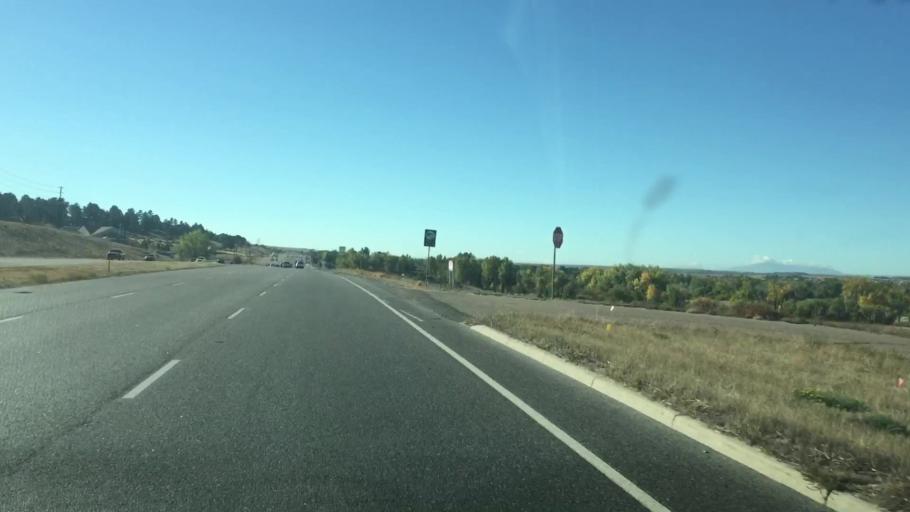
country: US
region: Colorado
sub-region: Douglas County
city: Parker
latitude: 39.5069
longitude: -104.7634
